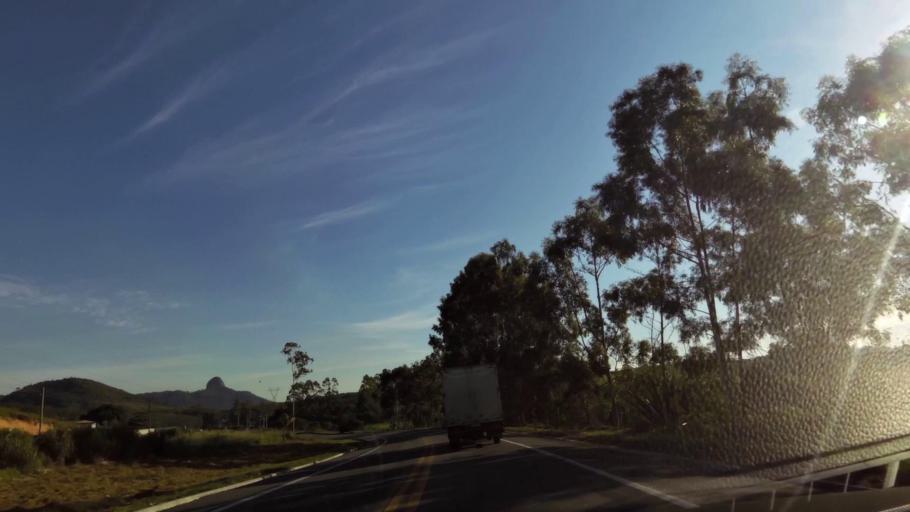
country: BR
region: Espirito Santo
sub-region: Guarapari
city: Guarapari
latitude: -20.5605
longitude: -40.4805
